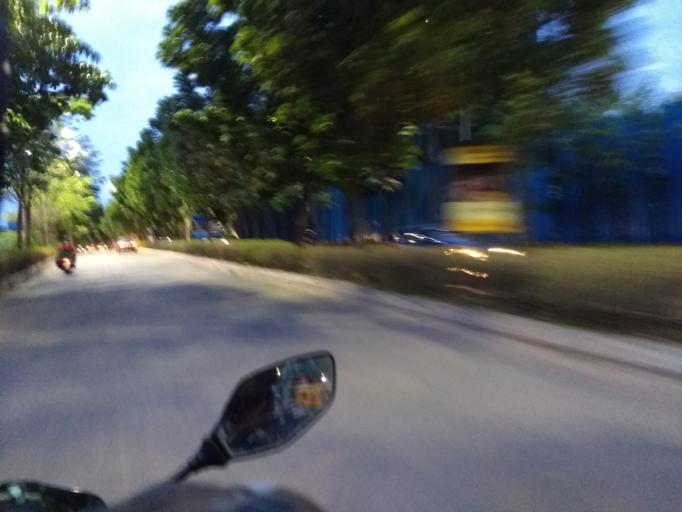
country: IN
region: Telangana
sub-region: Rangareddi
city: Kukatpalli
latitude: 17.4107
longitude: 78.3709
